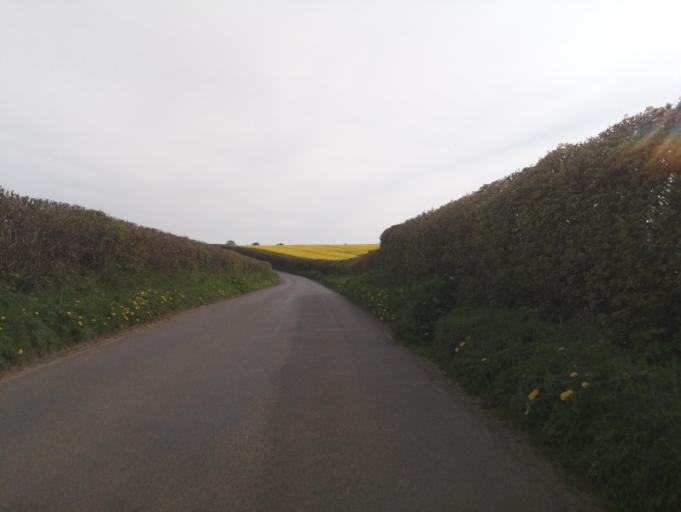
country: GB
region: England
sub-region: Dorset
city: Sherborne
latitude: 50.9831
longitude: -2.5162
